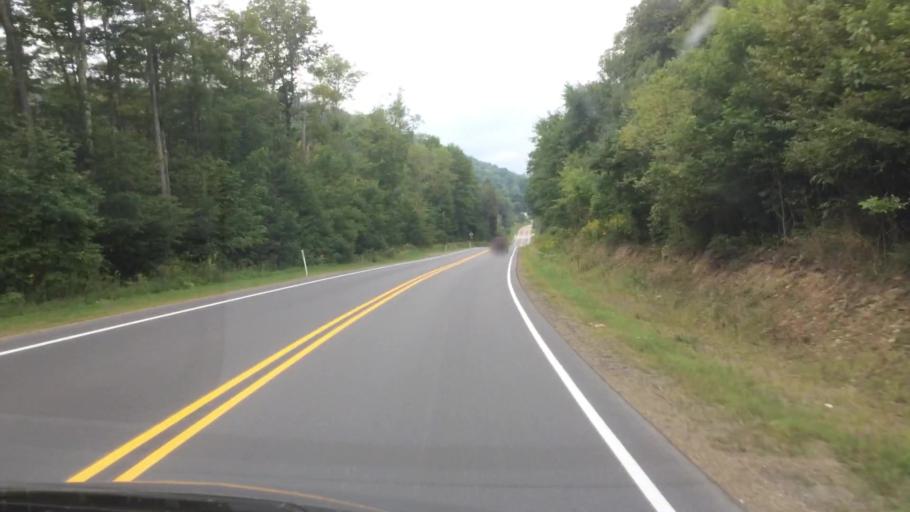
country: US
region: Pennsylvania
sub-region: McKean County
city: Bradford
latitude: 41.8882
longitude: -78.5993
